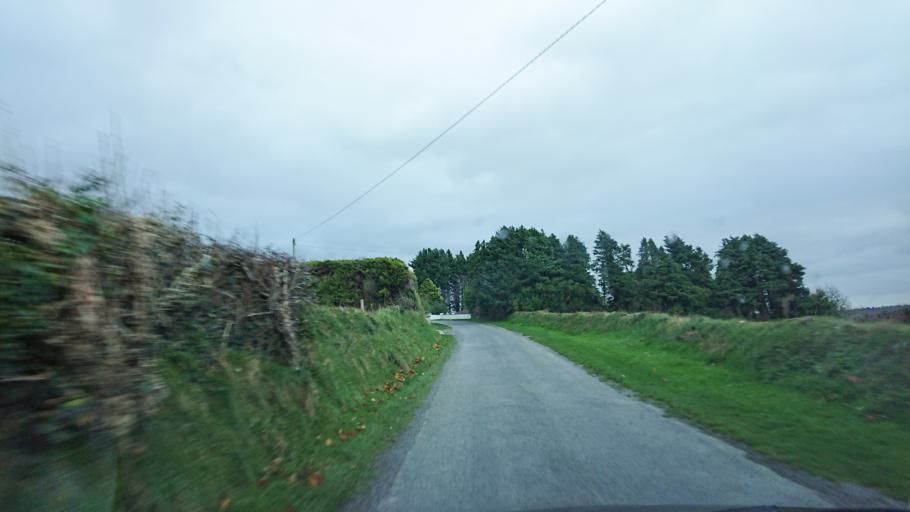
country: IE
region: Munster
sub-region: Waterford
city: Dunmore East
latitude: 52.2481
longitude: -7.0043
